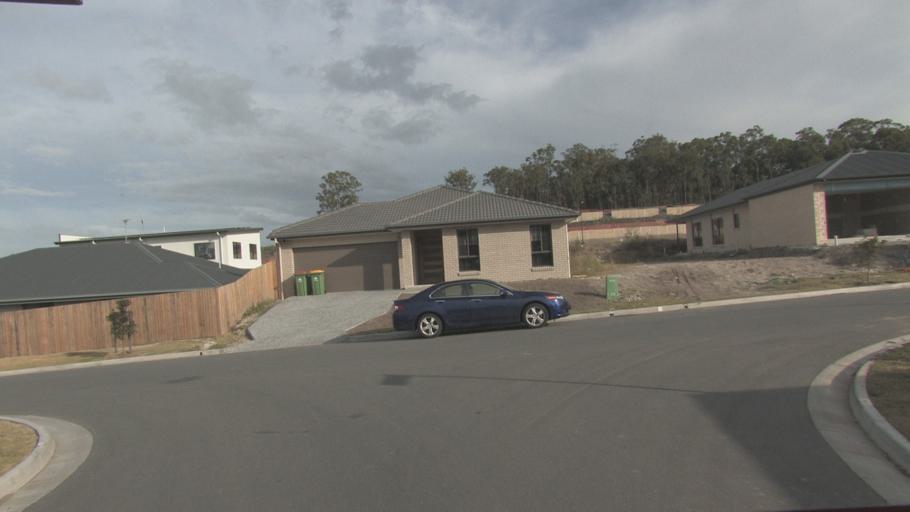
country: AU
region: Queensland
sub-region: Logan
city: Windaroo
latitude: -27.7200
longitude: 153.1616
